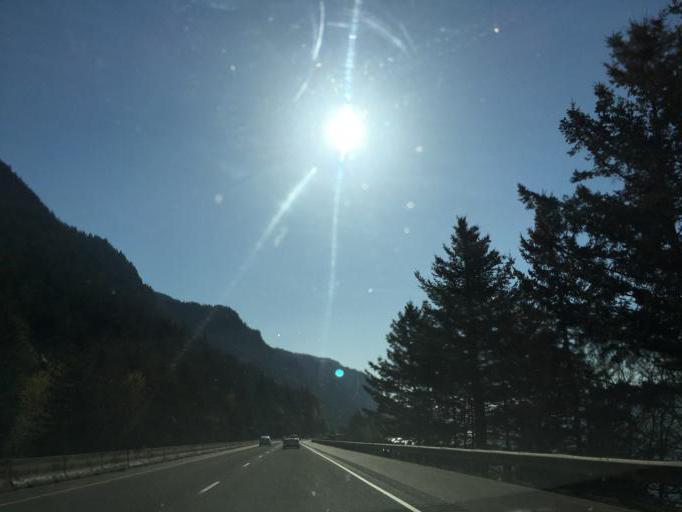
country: US
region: Oregon
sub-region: Hood River County
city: Cascade Locks
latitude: 45.5861
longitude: -122.0897
